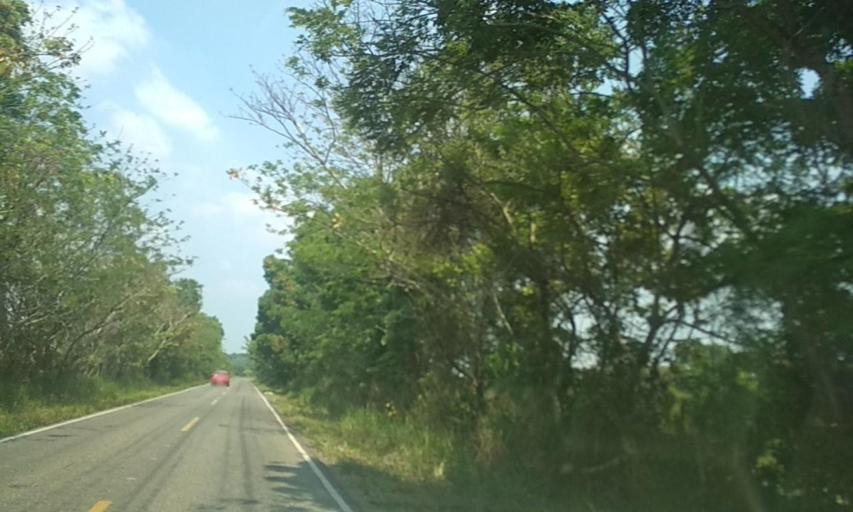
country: MX
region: Tabasco
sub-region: Huimanguillo
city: C-41 (Licenciado Carlos A. Madrazo)
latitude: 17.8486
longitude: -93.5359
